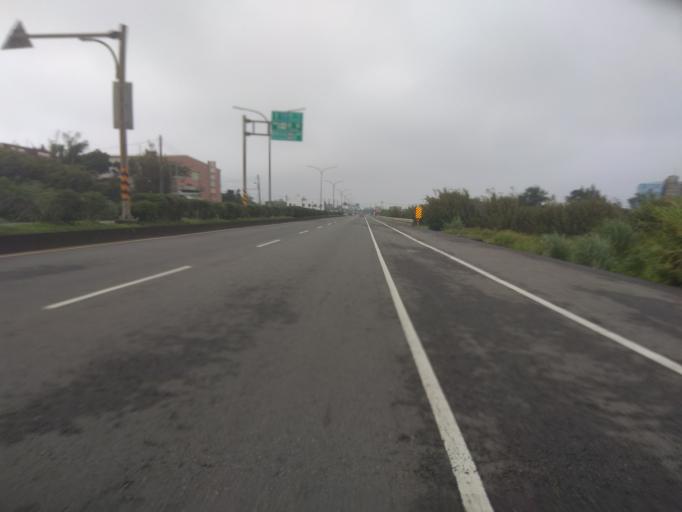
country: TW
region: Taiwan
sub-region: Hsinchu
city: Zhubei
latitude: 25.0274
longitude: 121.0896
